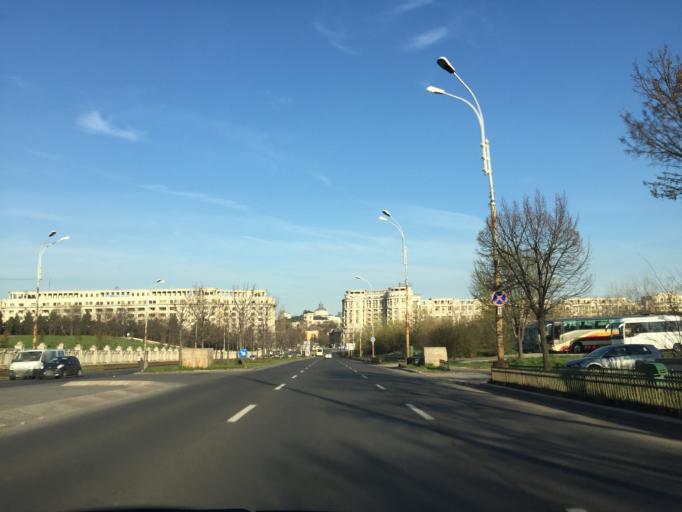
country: RO
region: Bucuresti
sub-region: Municipiul Bucuresti
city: Bucuresti
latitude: 44.4246
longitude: 26.0865
